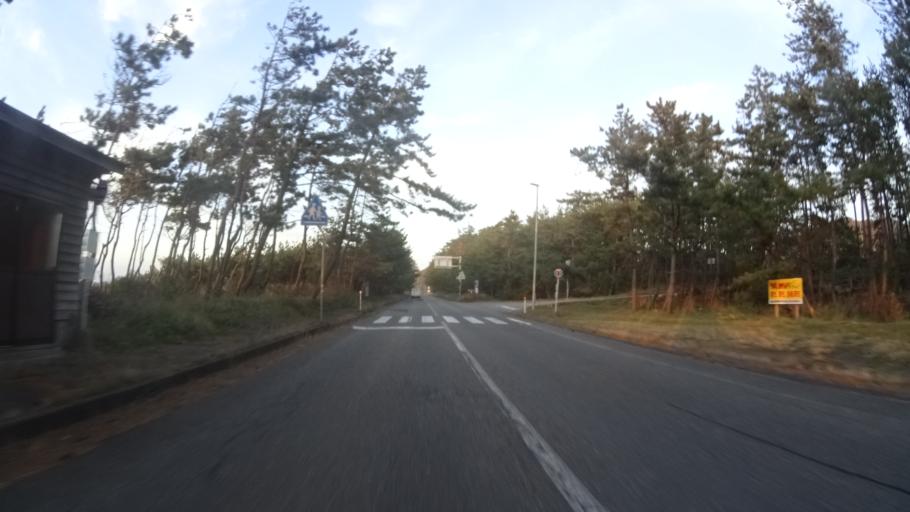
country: JP
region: Ishikawa
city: Nanao
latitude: 37.2573
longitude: 136.7228
